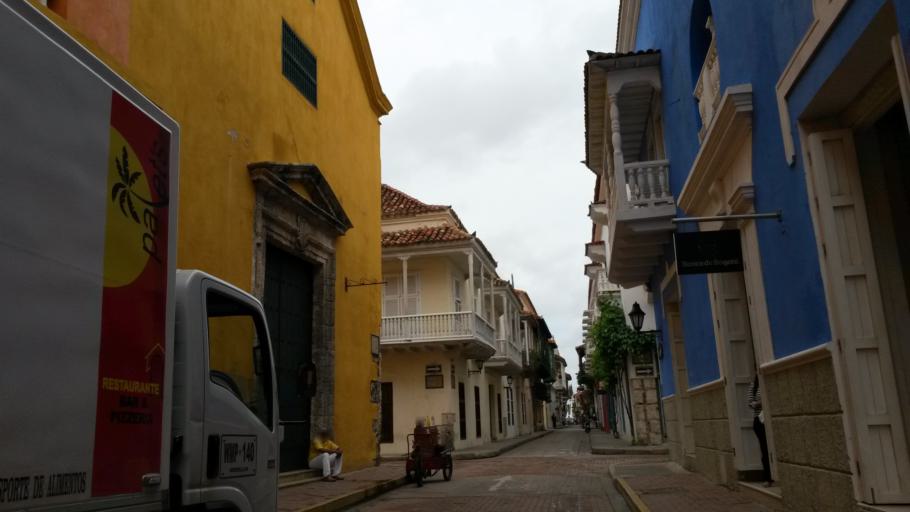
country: CO
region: Bolivar
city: Cartagena
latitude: 10.4223
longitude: -75.5524
